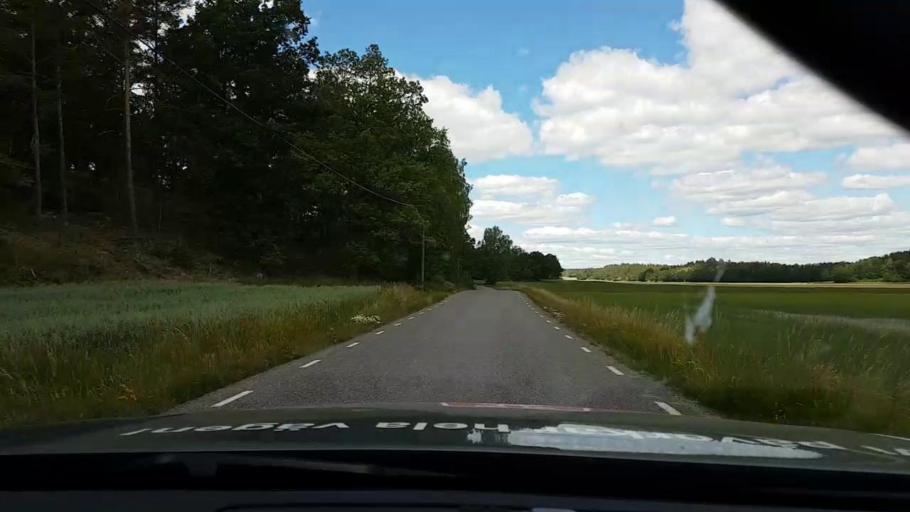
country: SE
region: Kalmar
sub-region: Vasterviks Kommun
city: Forserum
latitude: 57.9962
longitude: 16.5977
